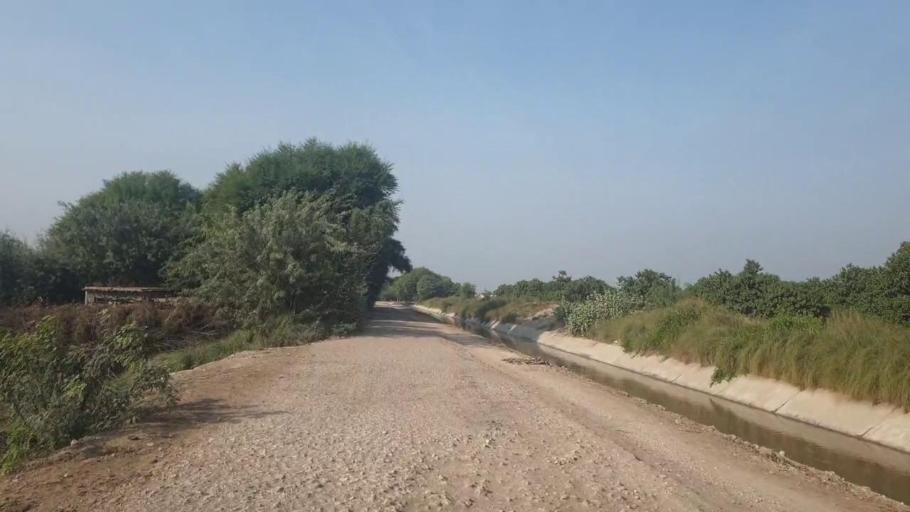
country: PK
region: Sindh
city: Tando Jam
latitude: 25.4133
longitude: 68.4651
